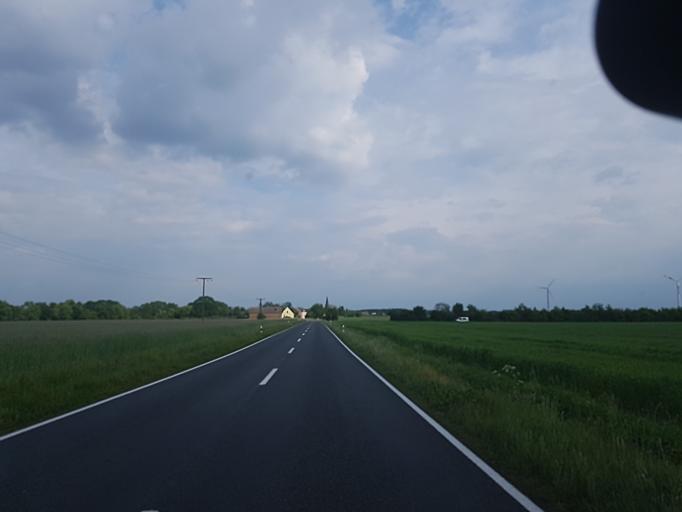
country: DE
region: Saxony-Anhalt
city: Klieken
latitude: 51.9166
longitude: 12.4035
